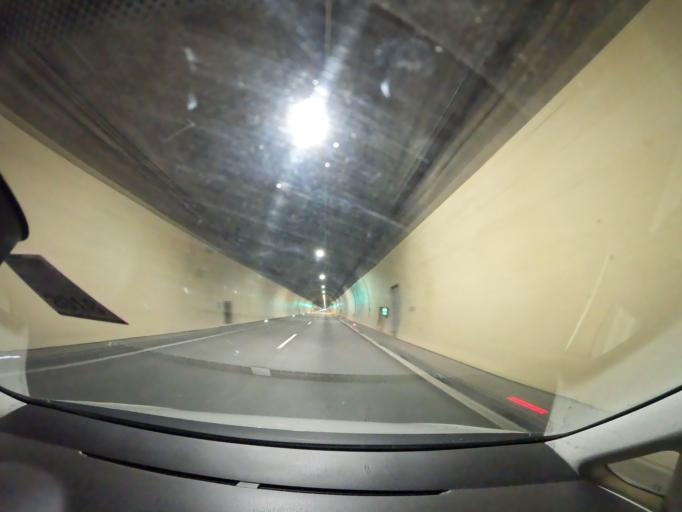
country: AT
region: Carinthia
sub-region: Politischer Bezirk Wolfsberg
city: Bad Sankt Leonhard im Lavanttal
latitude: 46.9078
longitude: 14.8230
